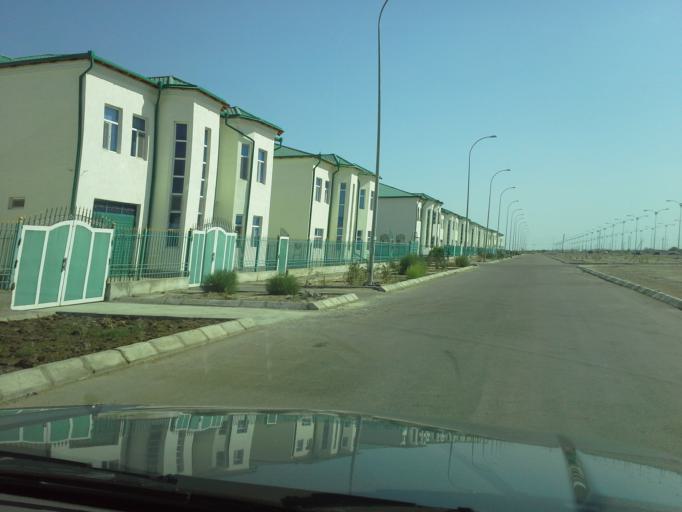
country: TM
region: Dasoguz
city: Dasoguz
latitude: 41.8082
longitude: 59.9522
